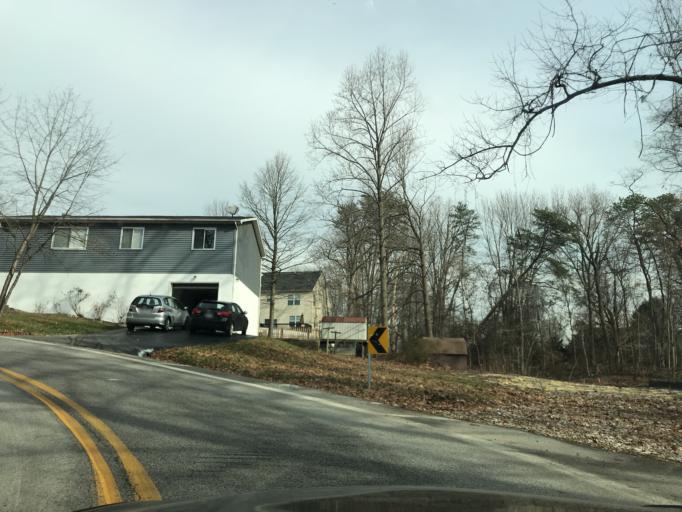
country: US
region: Maryland
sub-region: Howard County
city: Hanover
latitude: 39.1929
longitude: -76.7286
